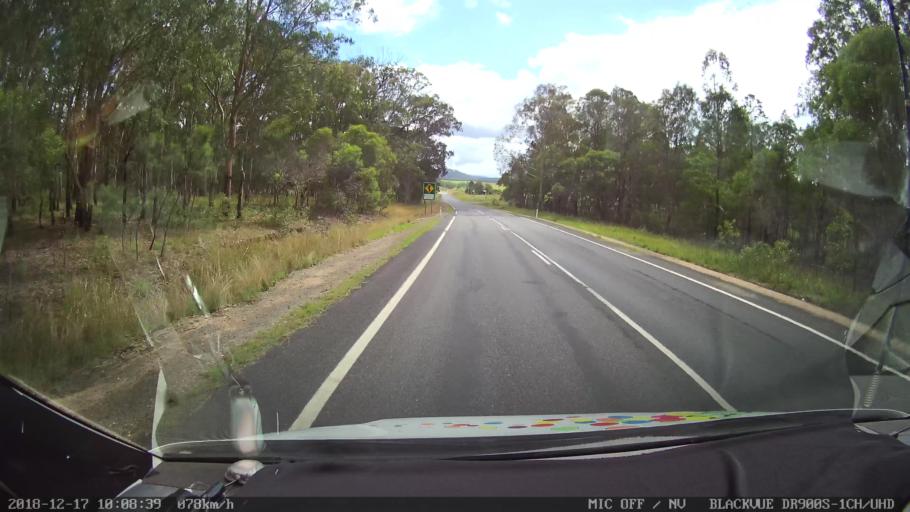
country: AU
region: New South Wales
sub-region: Tenterfield Municipality
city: Carrolls Creek
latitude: -28.8905
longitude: 152.5343
